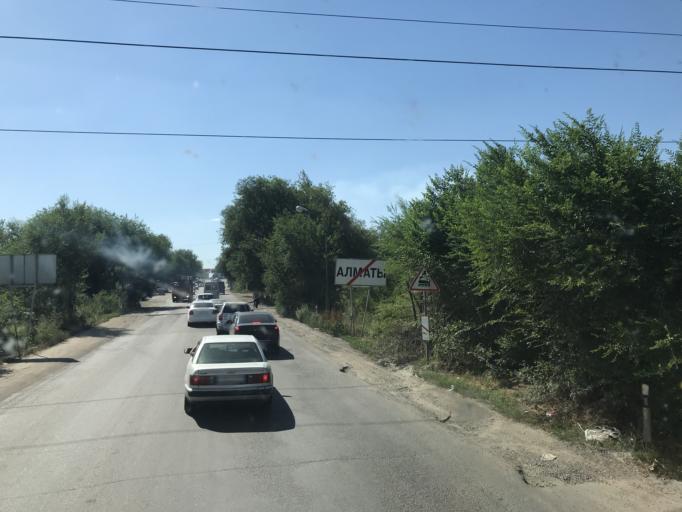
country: KZ
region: Almaty Oblysy
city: Pervomayskiy
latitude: 43.3551
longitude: 76.9136
